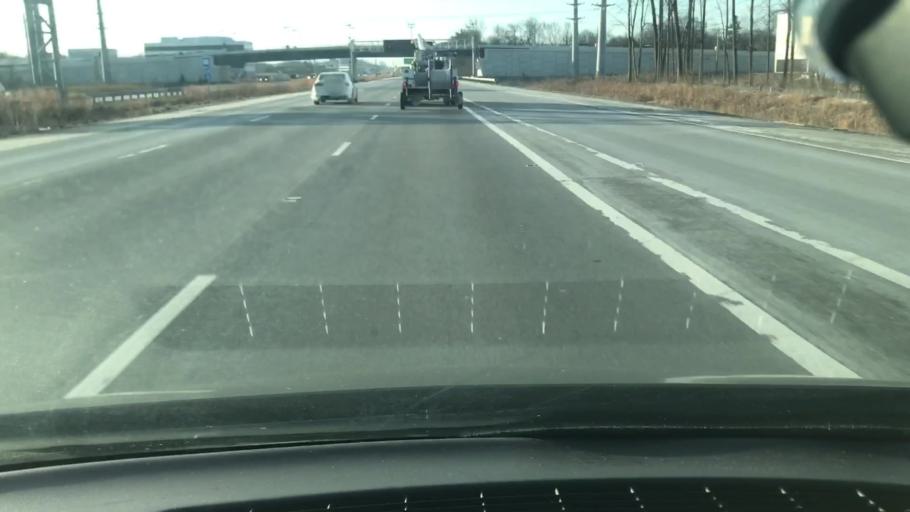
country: US
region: Indiana
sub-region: Hamilton County
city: Carmel
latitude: 39.9509
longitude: -86.1580
